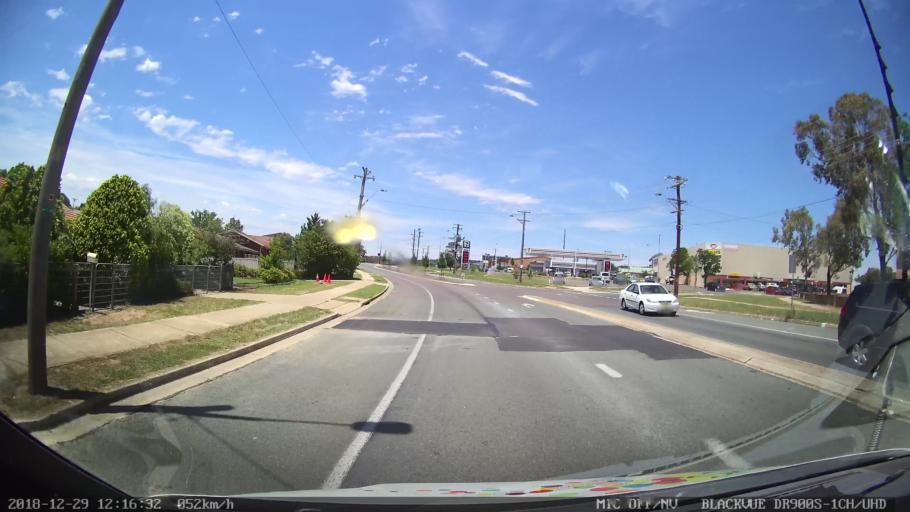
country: AU
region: New South Wales
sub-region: Queanbeyan
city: Queanbeyan
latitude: -35.3702
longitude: 149.2330
